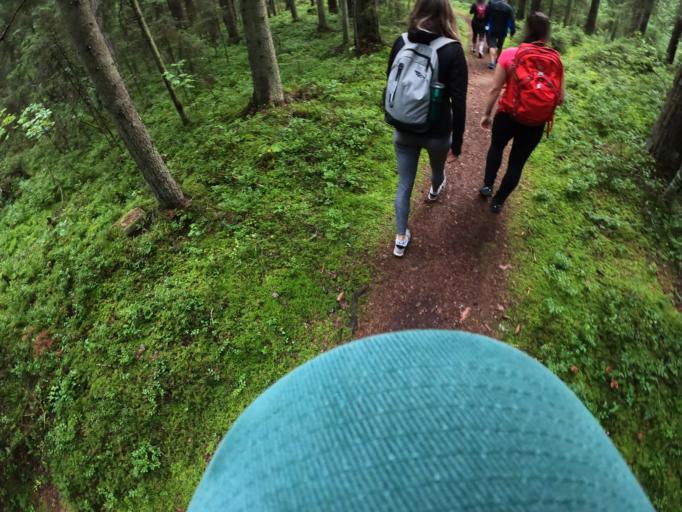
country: LV
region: Tukuma Rajons
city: Tukums
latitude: 56.9829
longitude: 23.1778
